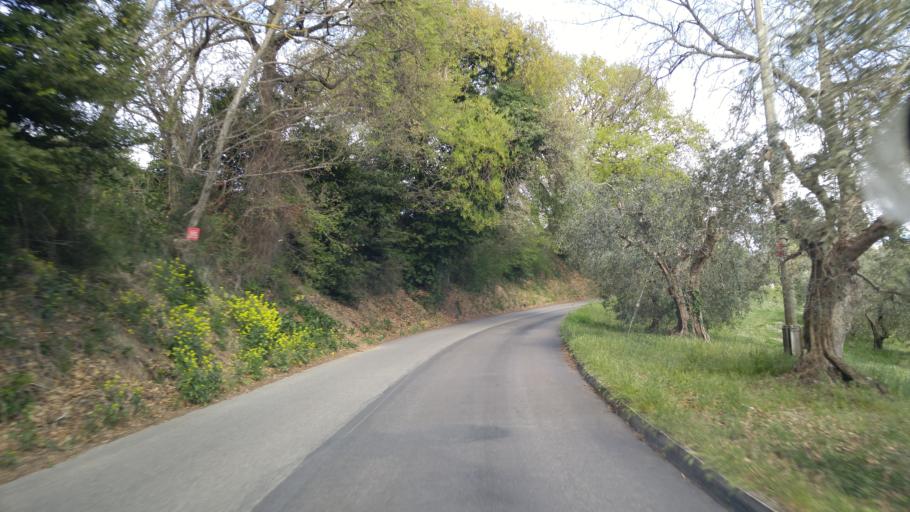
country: IT
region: The Marches
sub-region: Provincia di Pesaro e Urbino
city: Fenile
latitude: 43.8438
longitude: 12.9562
